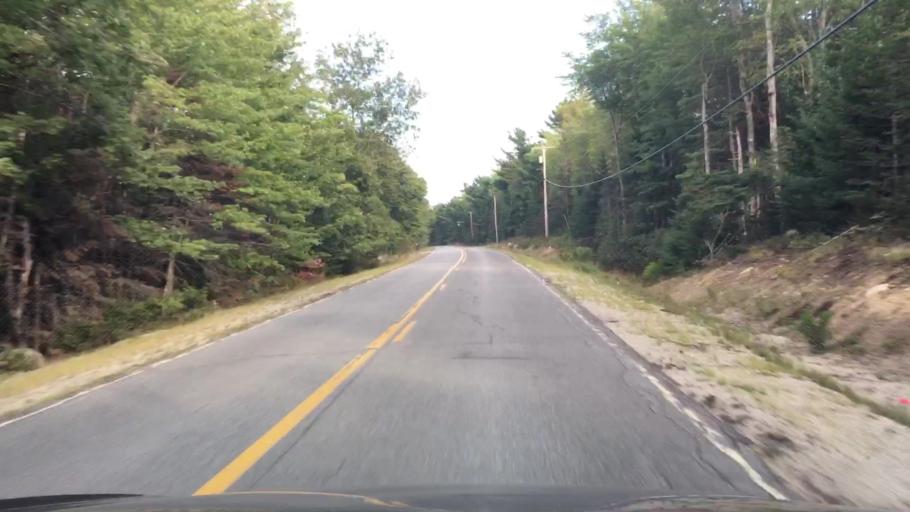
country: US
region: Maine
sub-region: Hancock County
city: Surry
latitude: 44.4987
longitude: -68.5463
